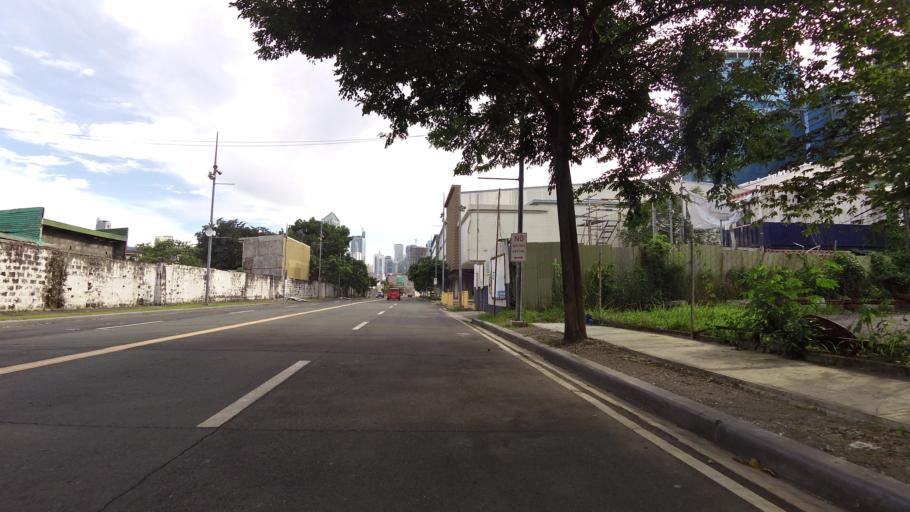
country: PH
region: Metro Manila
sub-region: Mandaluyong
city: Mandaluyong City
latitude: 14.5742
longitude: 121.0208
